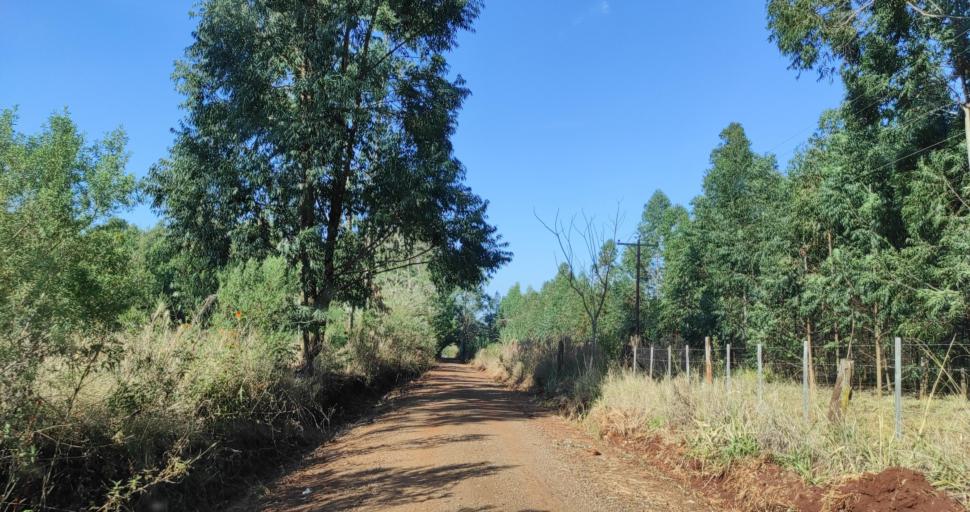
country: AR
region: Misiones
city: Capiovi
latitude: -26.8919
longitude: -55.0381
